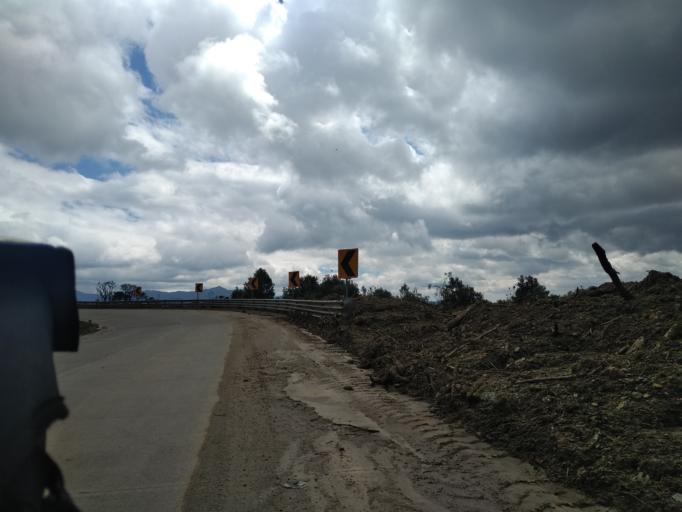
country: EC
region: Zamora-Chinchipe
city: Zamora
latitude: -4.4380
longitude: -79.1468
